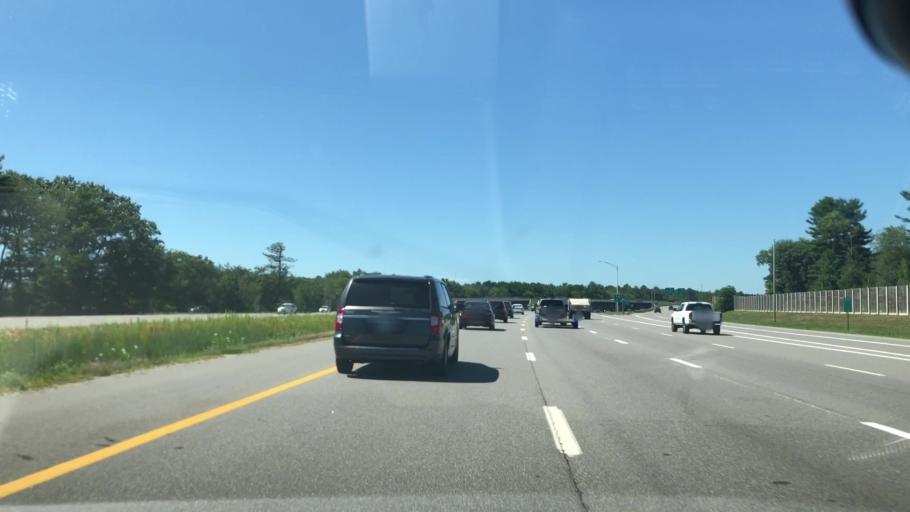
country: US
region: New Hampshire
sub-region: Rockingham County
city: Salem
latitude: 42.7576
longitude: -71.2285
